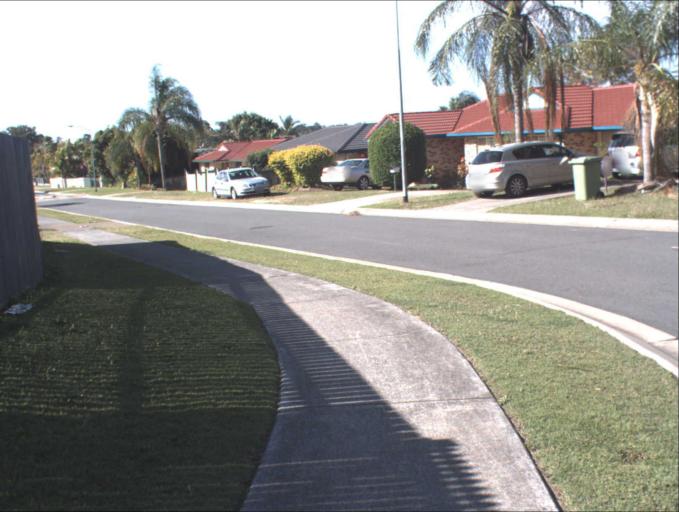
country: AU
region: Queensland
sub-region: Logan
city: Logan Reserve
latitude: -27.6964
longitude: 153.0804
